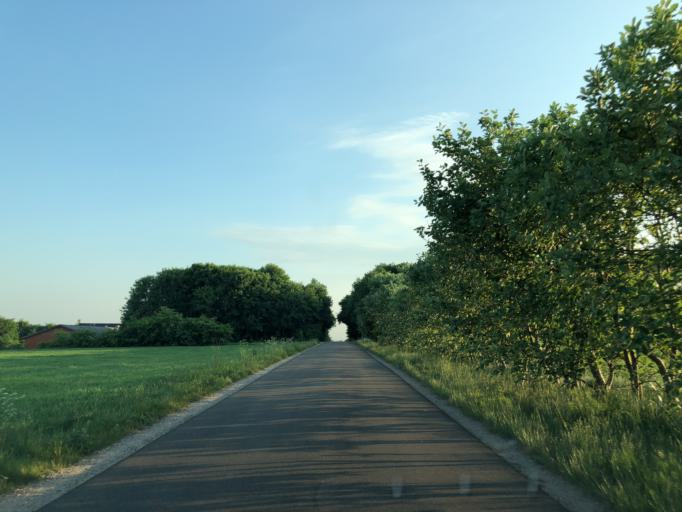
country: DK
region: Central Jutland
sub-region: Struer Kommune
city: Struer
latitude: 56.4212
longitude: 8.4952
